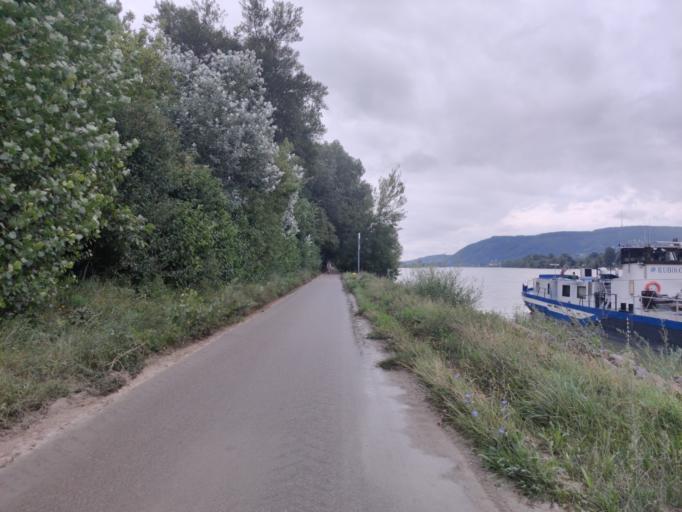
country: AT
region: Lower Austria
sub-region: Politischer Bezirk Korneuburg
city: Bisamberg
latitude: 48.3206
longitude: 16.3388
